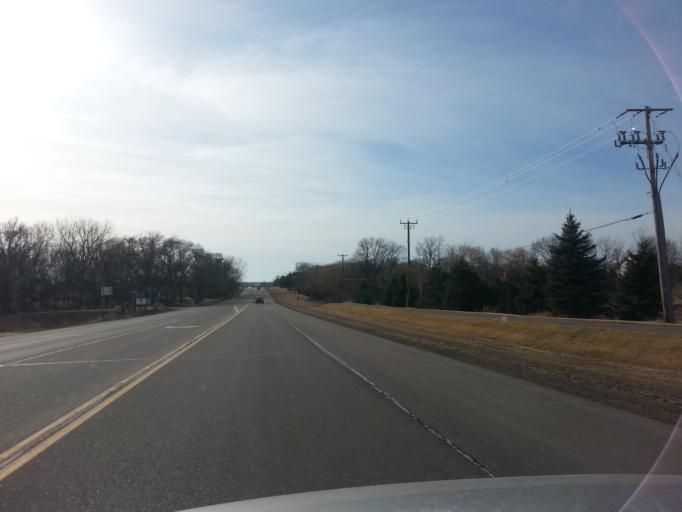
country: US
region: Minnesota
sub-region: Washington County
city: Woodbury
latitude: 44.8910
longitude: -92.8915
